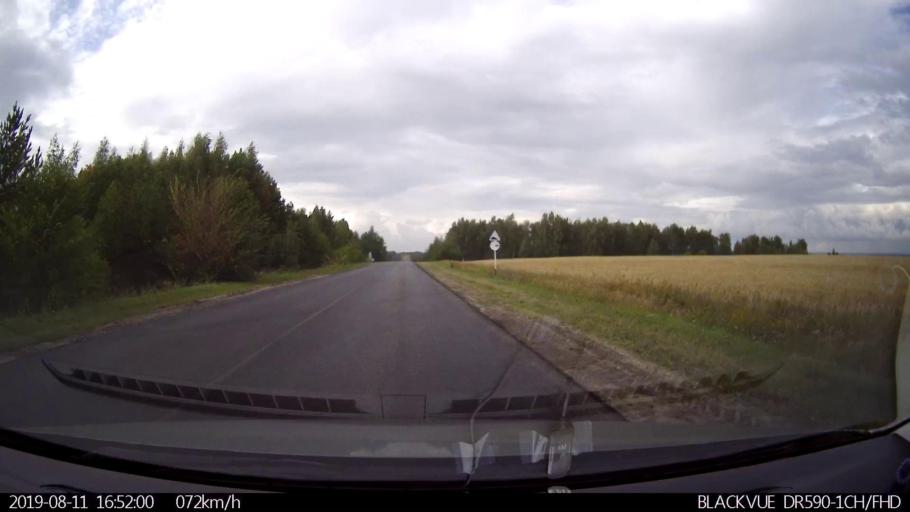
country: RU
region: Ulyanovsk
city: Mayna
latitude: 54.2430
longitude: 47.6754
